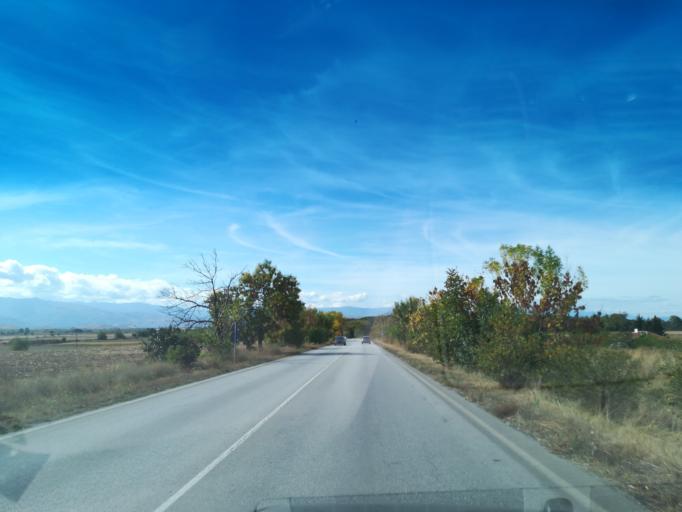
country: BG
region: Plovdiv
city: Stamboliyski
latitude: 42.1287
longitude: 24.5988
